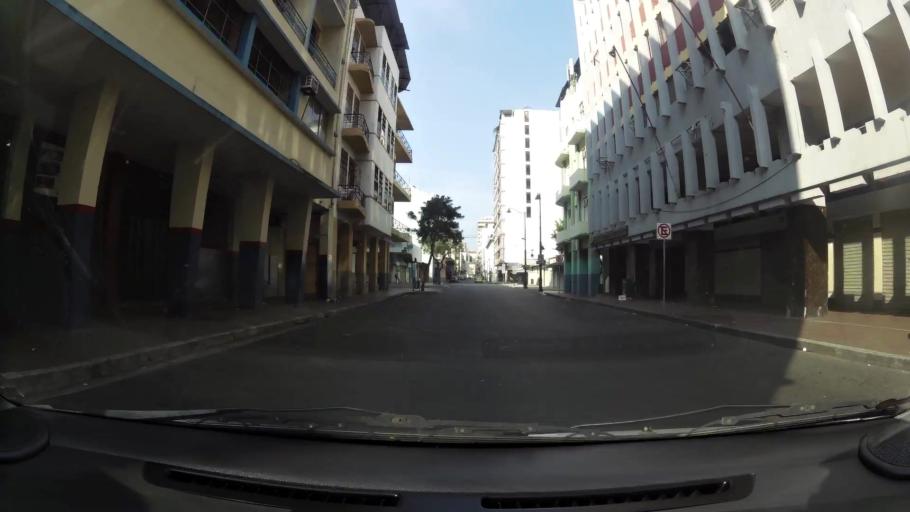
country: EC
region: Guayas
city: Guayaquil
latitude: -2.1901
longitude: -79.8831
